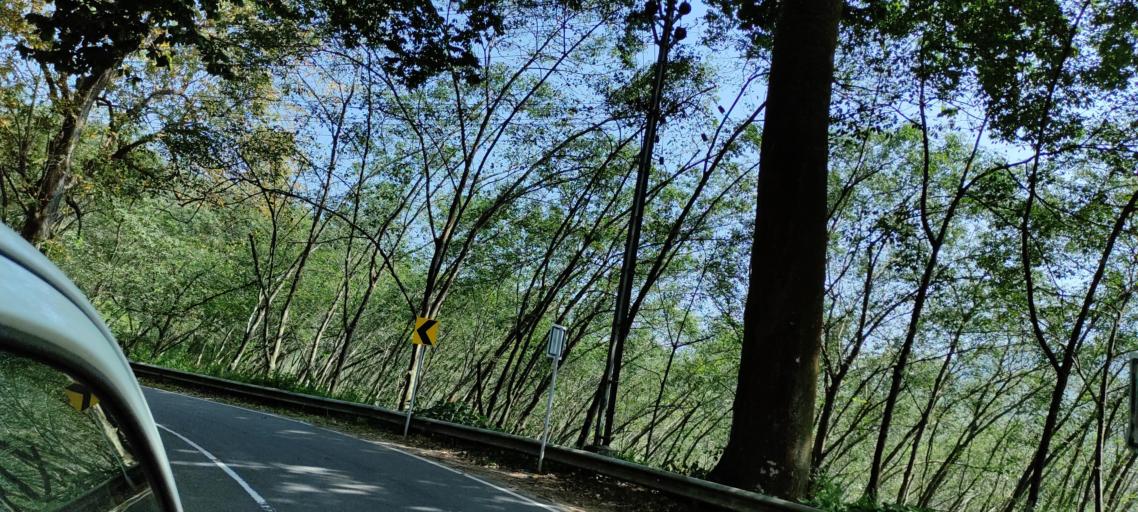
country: IN
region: Kerala
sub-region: Kollam
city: Punalur
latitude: 8.9738
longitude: 77.0613
